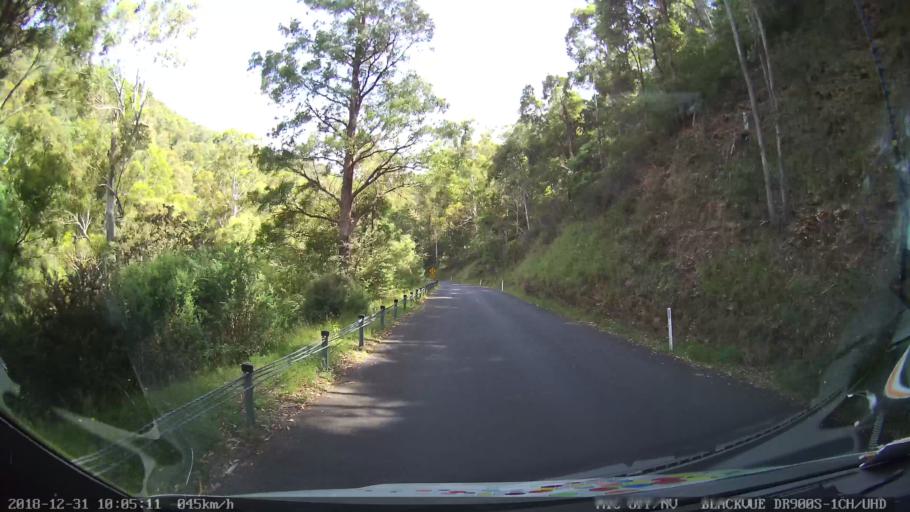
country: AU
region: New South Wales
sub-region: Snowy River
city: Jindabyne
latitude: -36.5276
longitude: 148.1938
